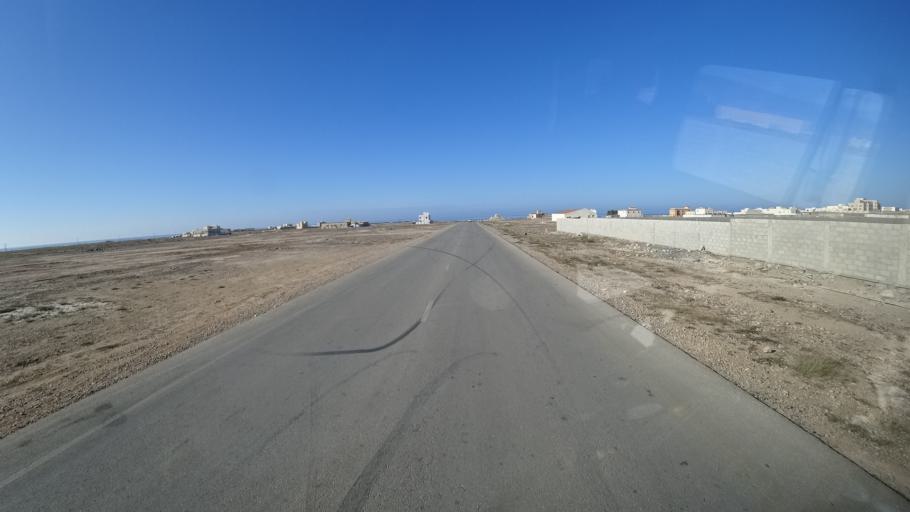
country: OM
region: Zufar
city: Salalah
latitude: 16.9797
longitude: 54.7028
